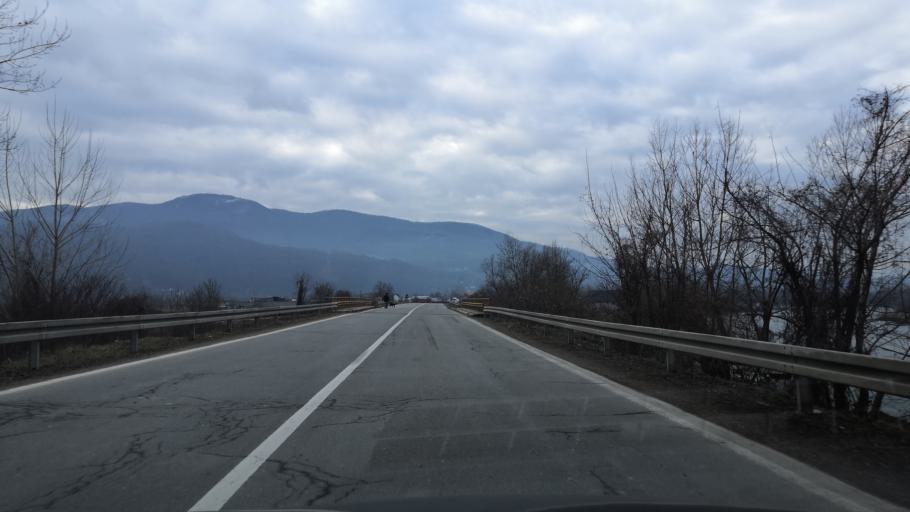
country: RS
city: Trsic
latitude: 44.5305
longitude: 19.1800
